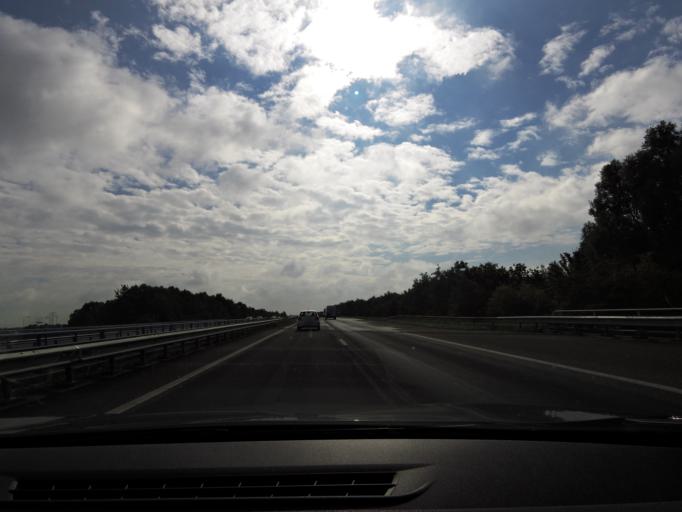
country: NL
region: Zeeland
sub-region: Gemeente Reimerswaal
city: Yerseke
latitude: 51.4378
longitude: 4.0658
